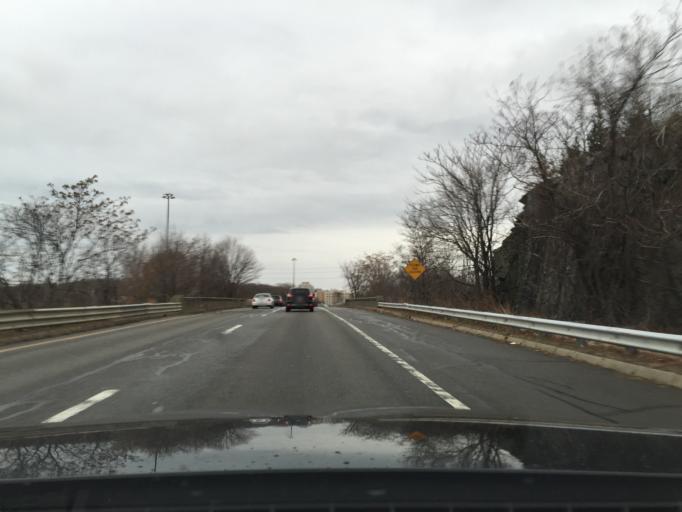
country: US
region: Massachusetts
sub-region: Essex County
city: Saugus
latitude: 42.4519
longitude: -71.0235
